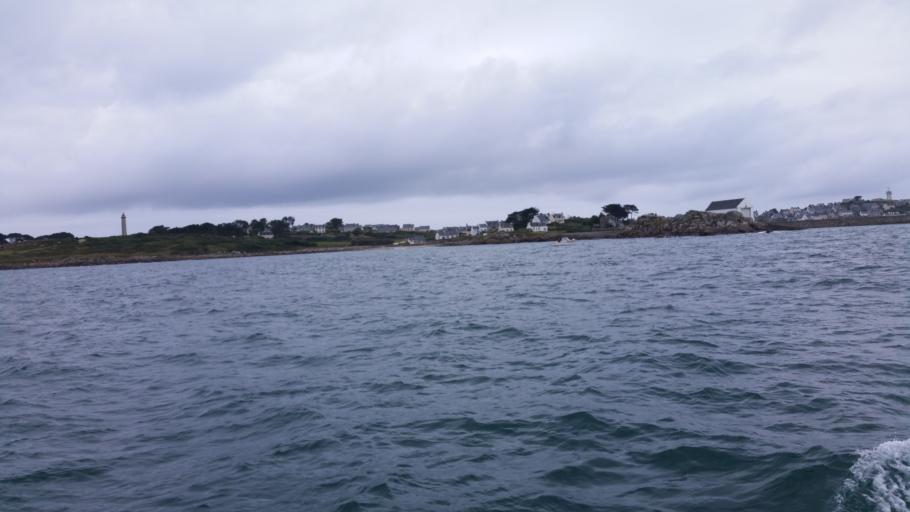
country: FR
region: Brittany
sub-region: Departement du Finistere
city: Roscoff
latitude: 48.7357
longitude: -4.0185
